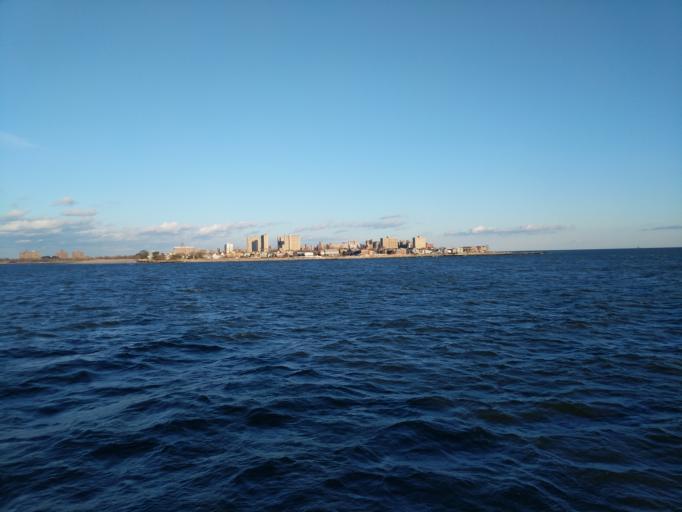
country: US
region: New York
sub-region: Kings County
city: Coney Island
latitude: 40.5789
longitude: -74.0205
